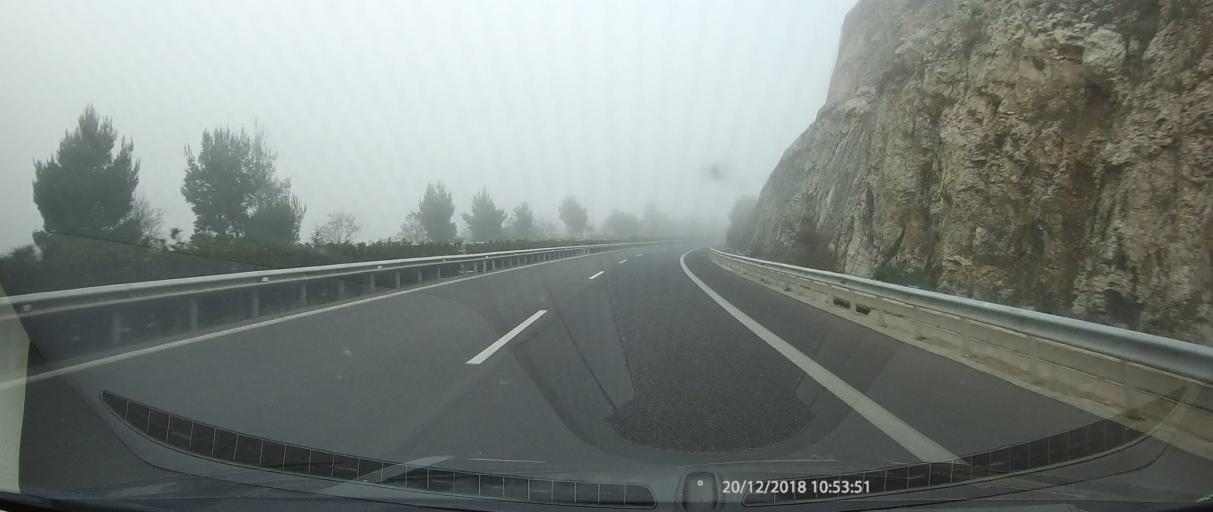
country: GR
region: Peloponnese
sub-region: Nomos Arkadias
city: Tripoli
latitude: 37.6164
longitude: 22.4581
